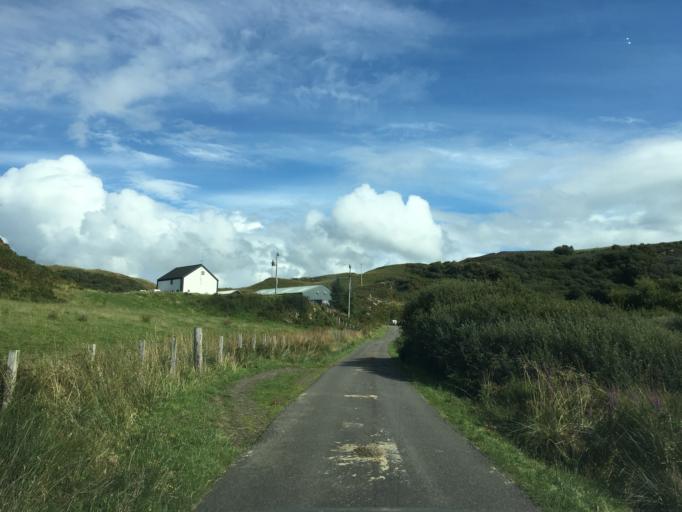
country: GB
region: Scotland
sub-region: Argyll and Bute
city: Oban
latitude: 56.2473
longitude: -5.6413
